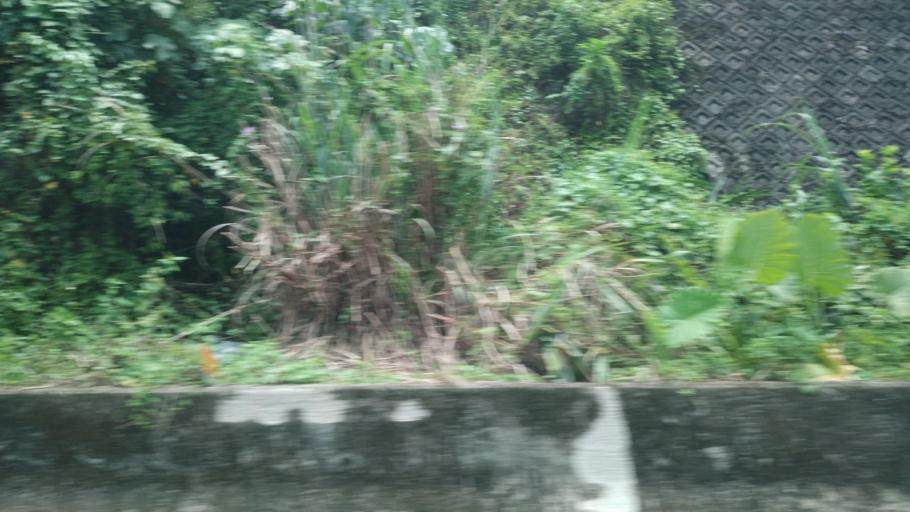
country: TW
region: Taipei
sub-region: Taipei
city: Banqiao
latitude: 24.9395
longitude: 121.4649
